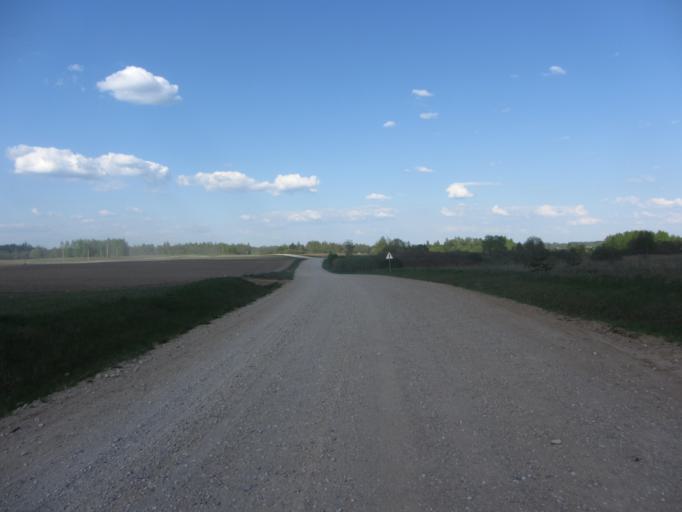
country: LT
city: Pabrade
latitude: 55.1081
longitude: 25.6888
